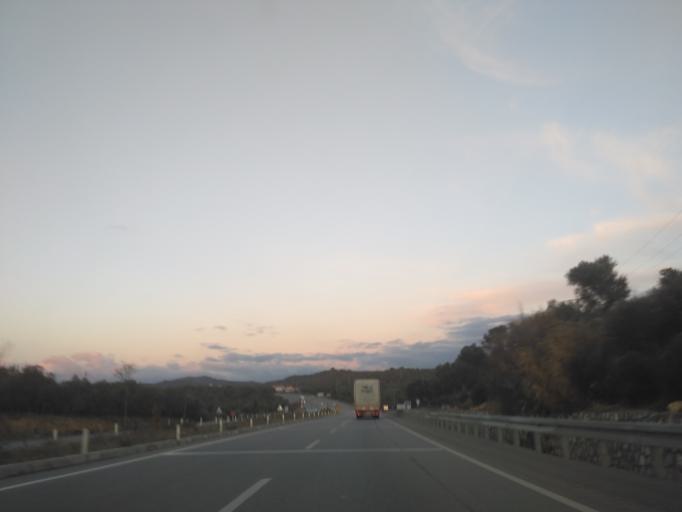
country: TR
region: Balikesir
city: Emrutabat
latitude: 39.4484
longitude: 26.8772
